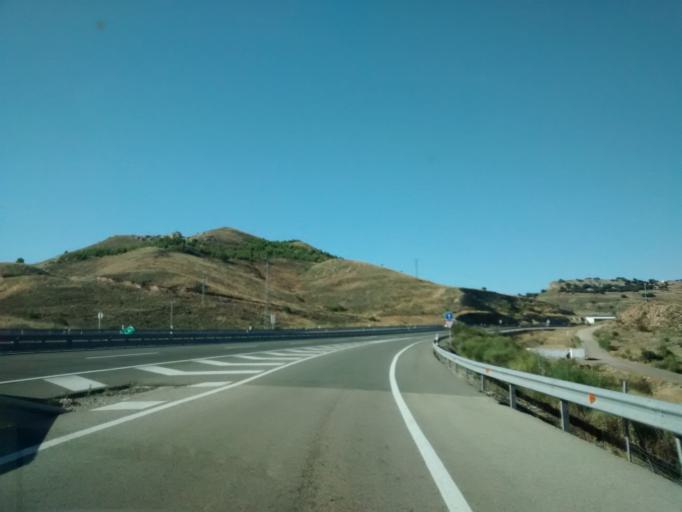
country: ES
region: Castille and Leon
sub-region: Provincia de Soria
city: Medinaceli
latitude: 41.1905
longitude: -2.4024
